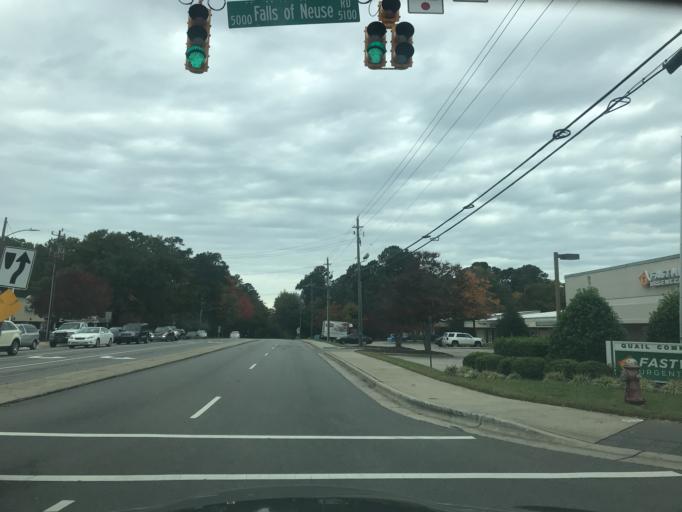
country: US
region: North Carolina
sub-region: Wake County
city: West Raleigh
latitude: 35.8507
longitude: -78.6145
